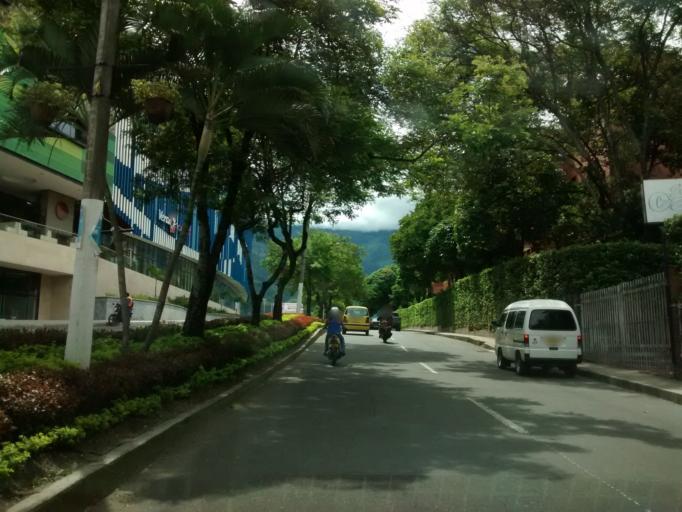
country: CO
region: Tolima
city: Ibague
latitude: 4.4398
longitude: -75.2039
